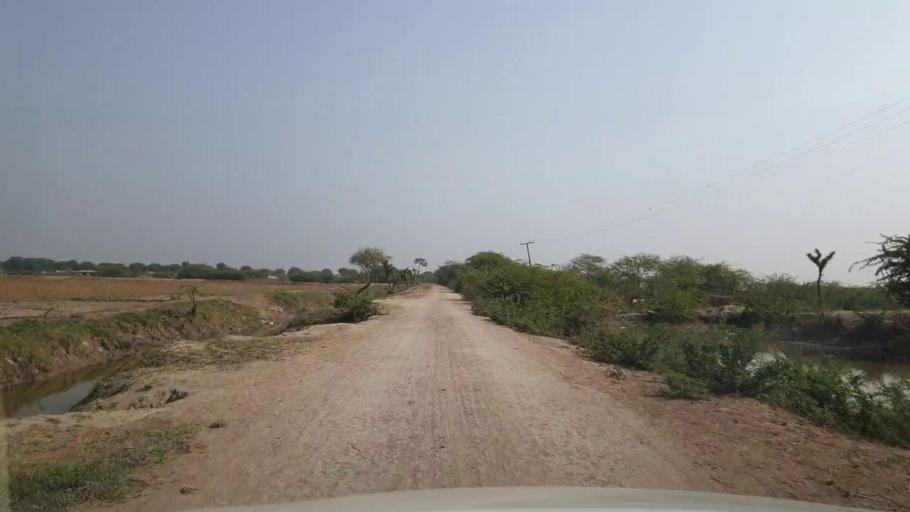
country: PK
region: Sindh
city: Umarkot
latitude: 25.4397
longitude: 69.7231
